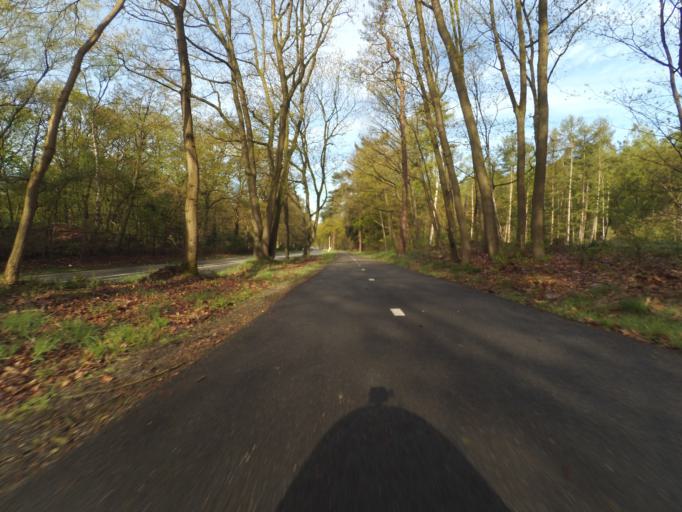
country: NL
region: Utrecht
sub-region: Gemeente Utrechtse Heuvelrug
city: Doorn
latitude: 52.0345
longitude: 5.3584
